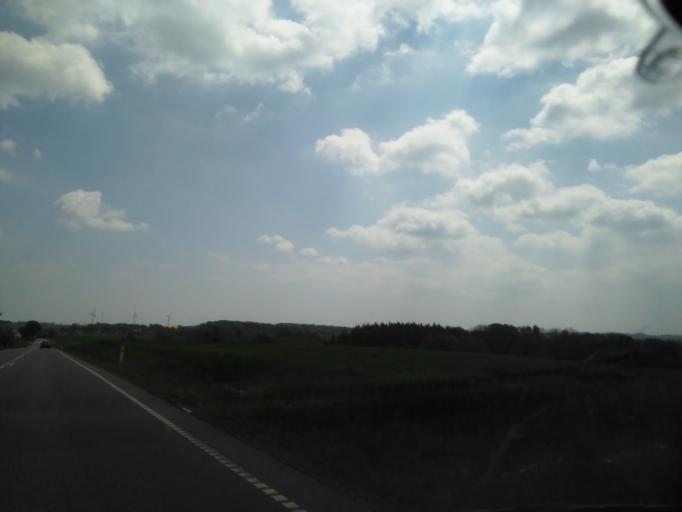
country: DK
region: Central Jutland
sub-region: Skanderborg Kommune
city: Stilling
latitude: 55.9979
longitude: 10.0113
